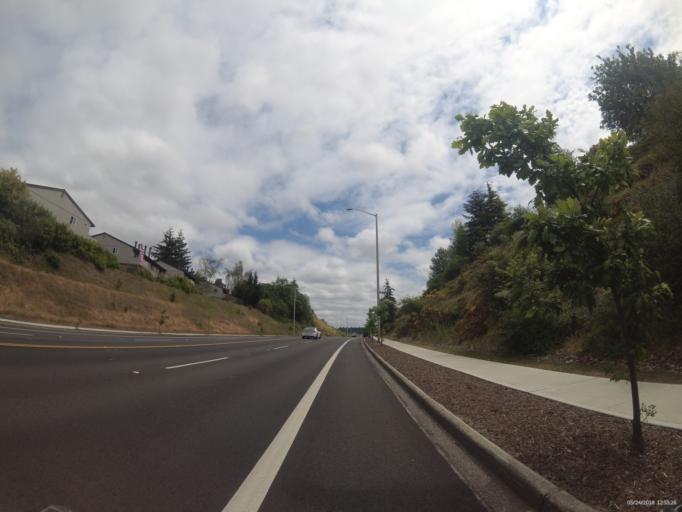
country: US
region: Washington
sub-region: Pierce County
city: Fircrest
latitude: 47.2065
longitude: -122.4975
